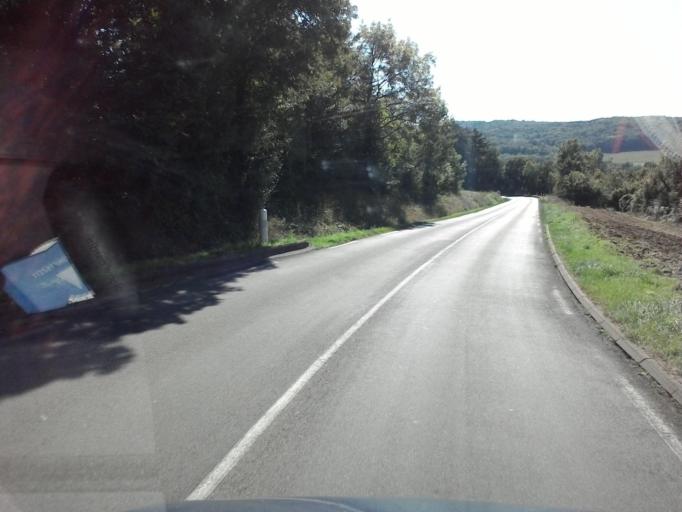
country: FR
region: Bourgogne
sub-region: Departement de l'Yonne
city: Joux-la-Ville
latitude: 47.5672
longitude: 3.8868
